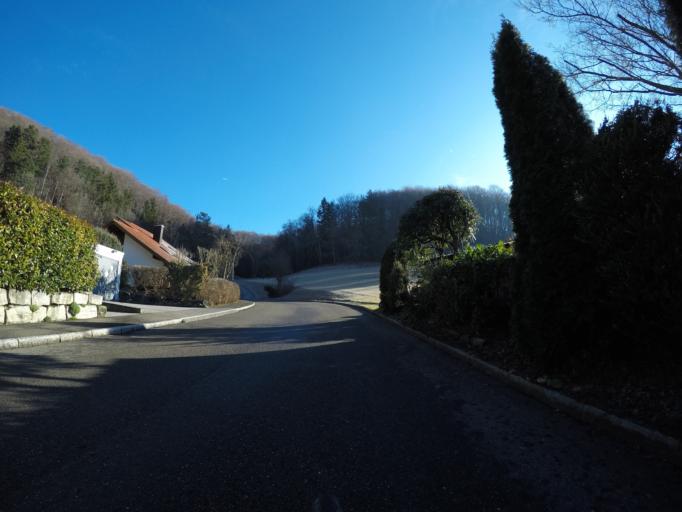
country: DE
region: Baden-Wuerttemberg
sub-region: Tuebingen Region
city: Pfullingen
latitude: 48.4476
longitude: 9.2607
